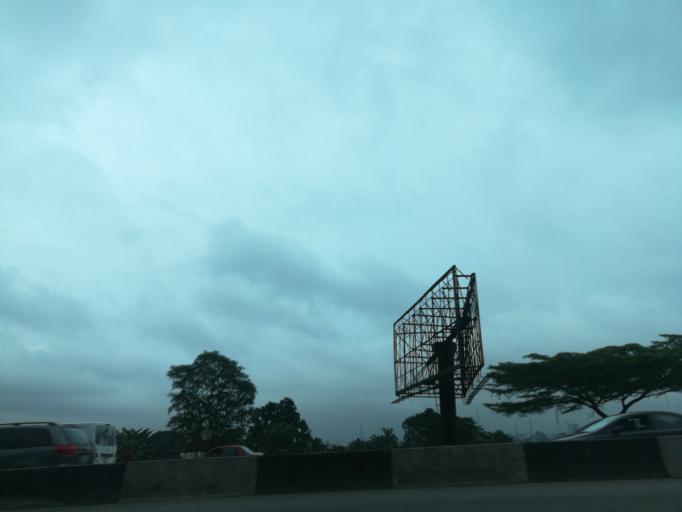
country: NG
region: Rivers
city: Port Harcourt
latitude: 4.8103
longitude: 7.0100
